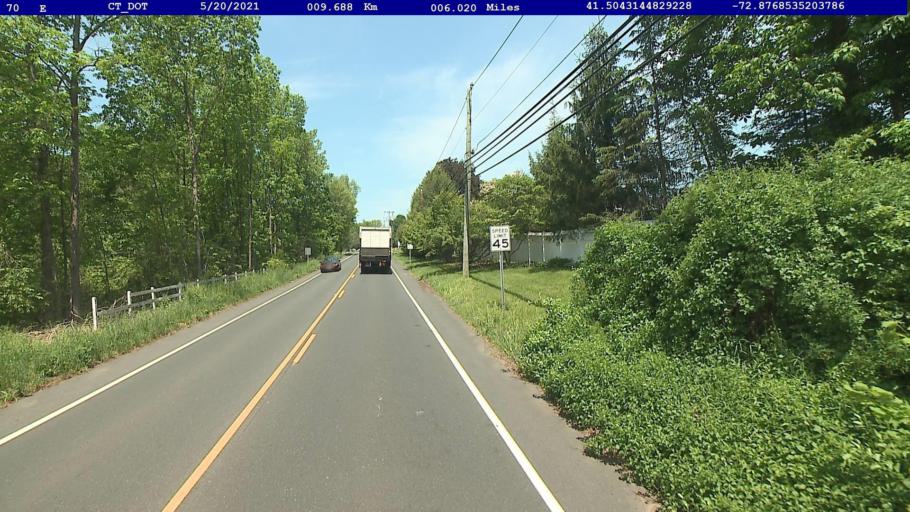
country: US
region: Connecticut
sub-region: New Haven County
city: Cheshire Village
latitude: 41.5038
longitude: -72.8764
